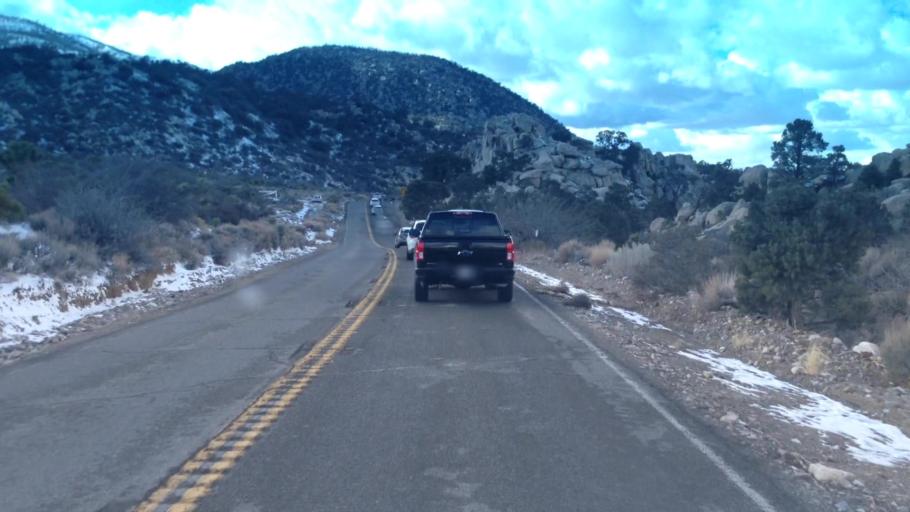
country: US
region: California
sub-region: San Bernardino County
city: Big Bear City
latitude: 34.3168
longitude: -116.8135
